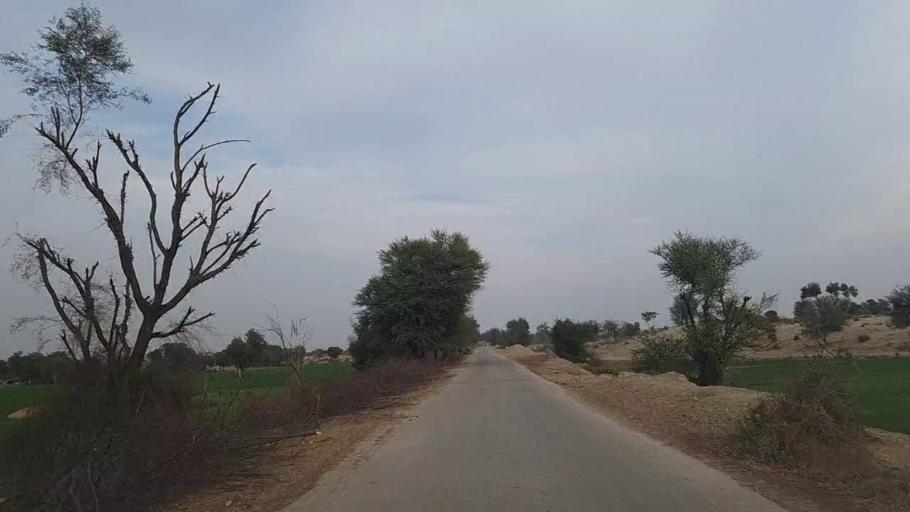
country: PK
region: Sindh
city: Daur
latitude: 26.5150
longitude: 68.4757
